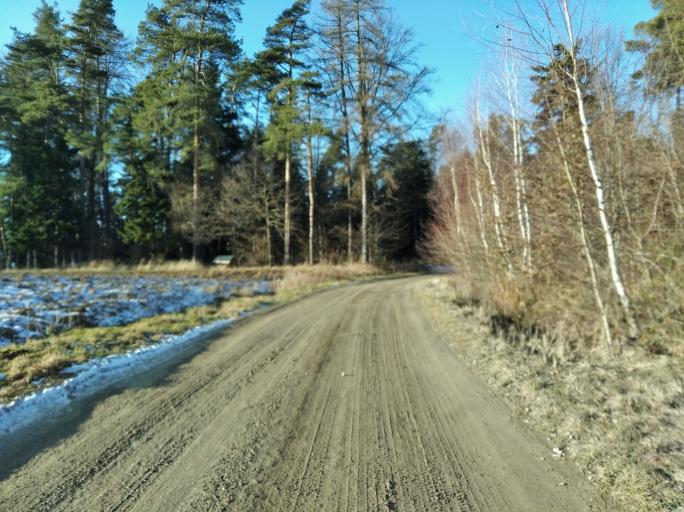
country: PL
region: Subcarpathian Voivodeship
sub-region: Powiat strzyzowski
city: Jawornik
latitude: 49.8312
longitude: 21.8591
